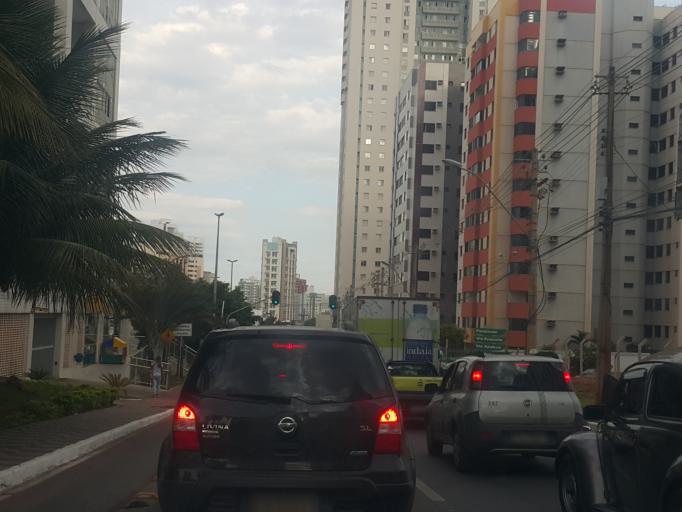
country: BR
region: Federal District
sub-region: Brasilia
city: Brasilia
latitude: -15.8398
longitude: -48.0353
